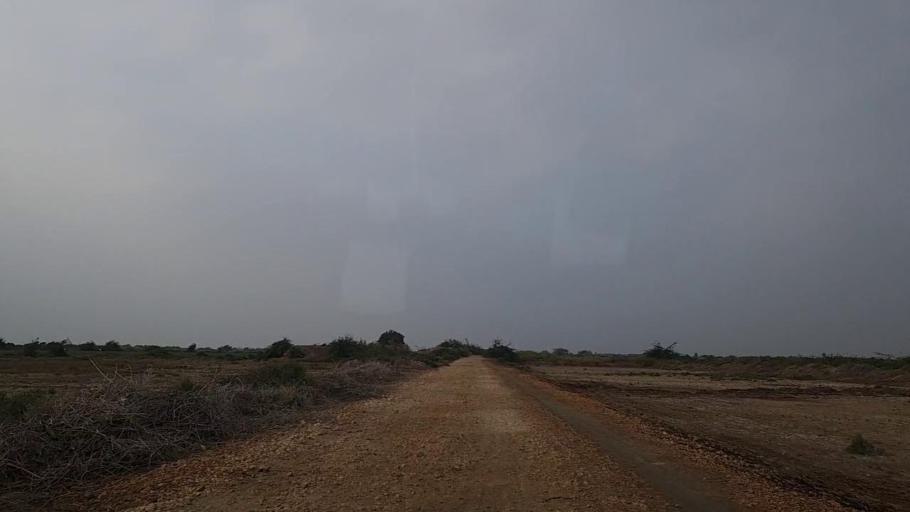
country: PK
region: Sindh
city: Mirpur Sakro
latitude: 24.6080
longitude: 67.5158
